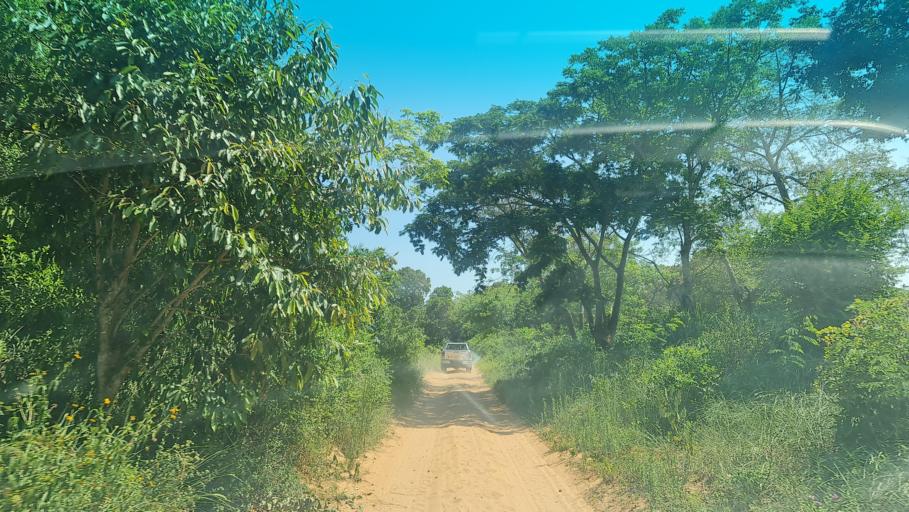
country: MZ
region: Gaza
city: Macia
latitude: -25.0892
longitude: 33.0978
